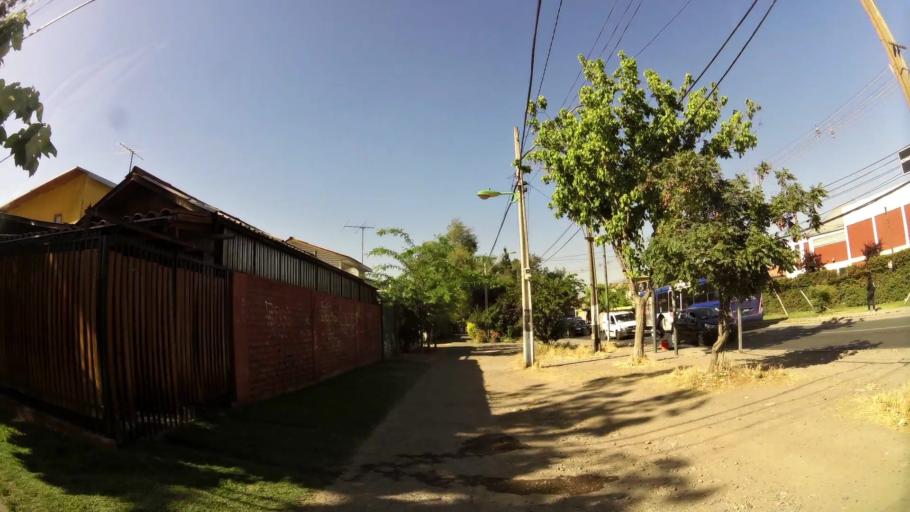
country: CL
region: Santiago Metropolitan
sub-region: Provincia de Maipo
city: San Bernardo
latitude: -33.5669
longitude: -70.6980
